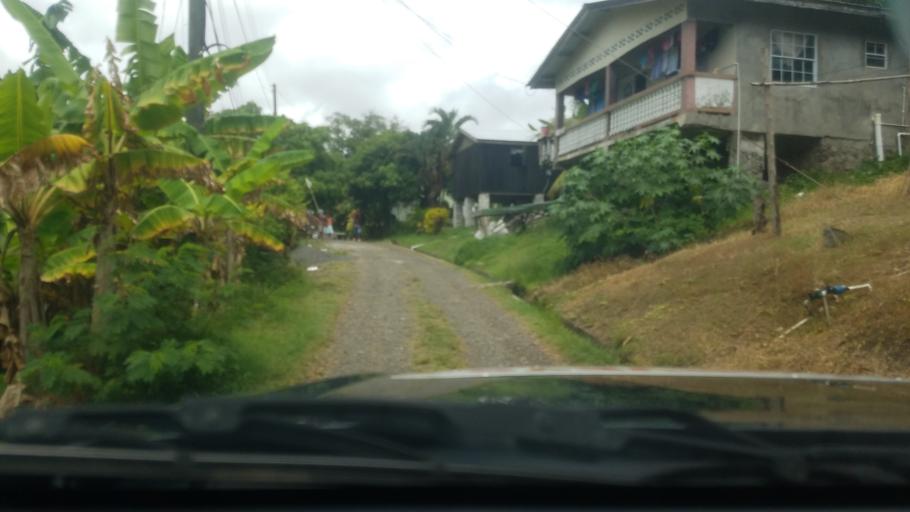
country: LC
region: Praslin
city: Praslin
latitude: 13.8749
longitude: -60.8971
